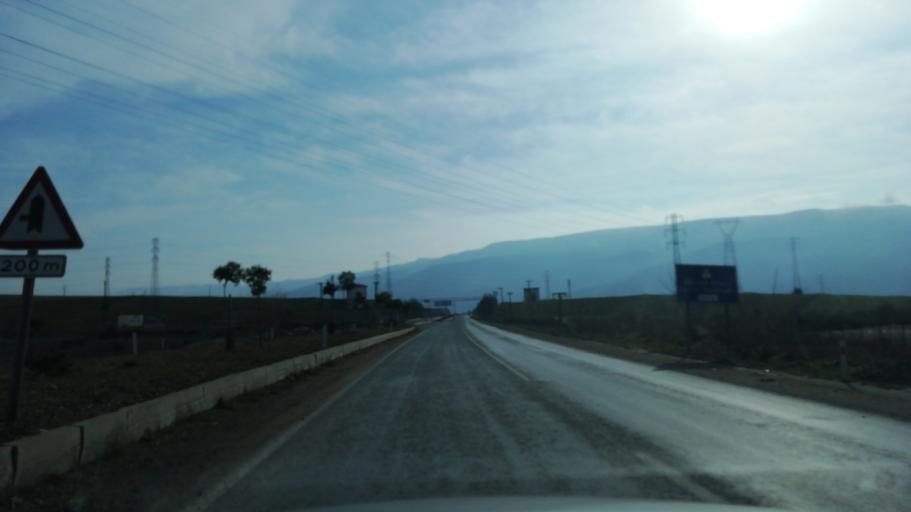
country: TR
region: Karabuk
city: Safranbolu
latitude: 41.2398
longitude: 32.7008
